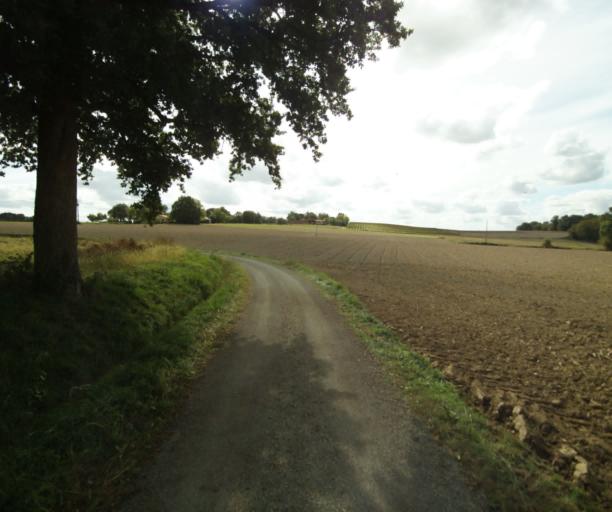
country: FR
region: Midi-Pyrenees
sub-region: Departement du Gers
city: Eauze
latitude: 43.8333
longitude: 0.1707
